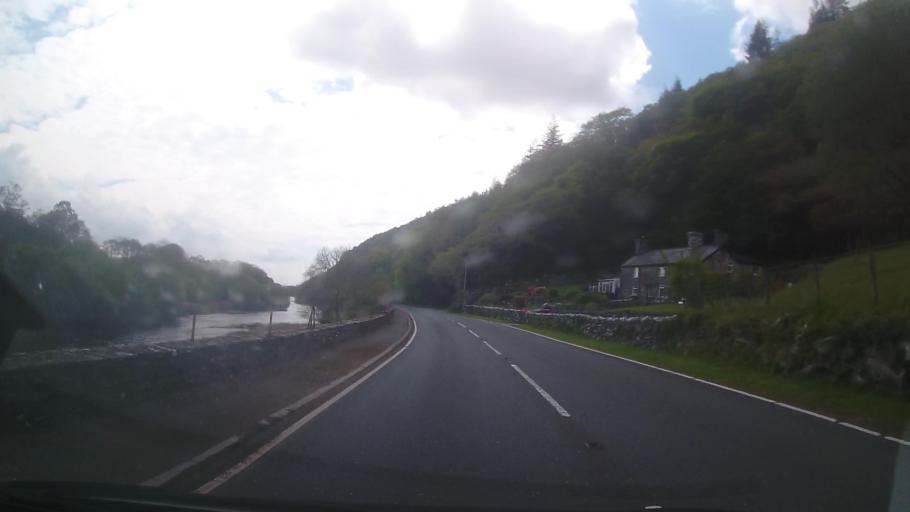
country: GB
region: Wales
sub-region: Gwynedd
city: Penrhyndeudraeth
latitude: 52.9846
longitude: -4.0943
